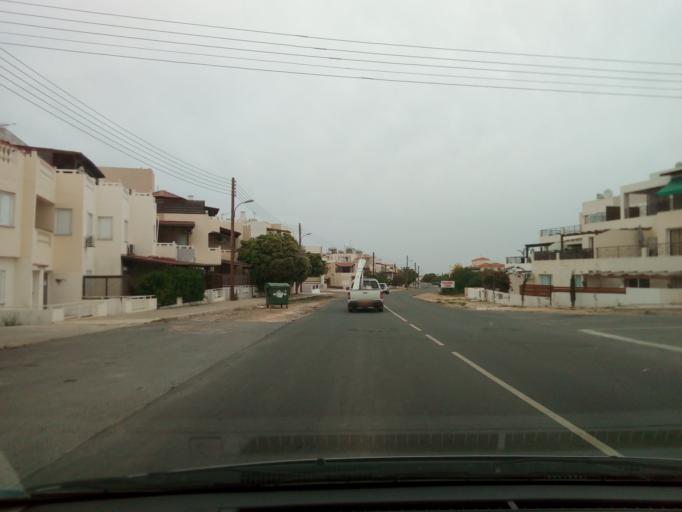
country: CY
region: Ammochostos
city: Paralimni
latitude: 35.0547
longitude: 33.9984
